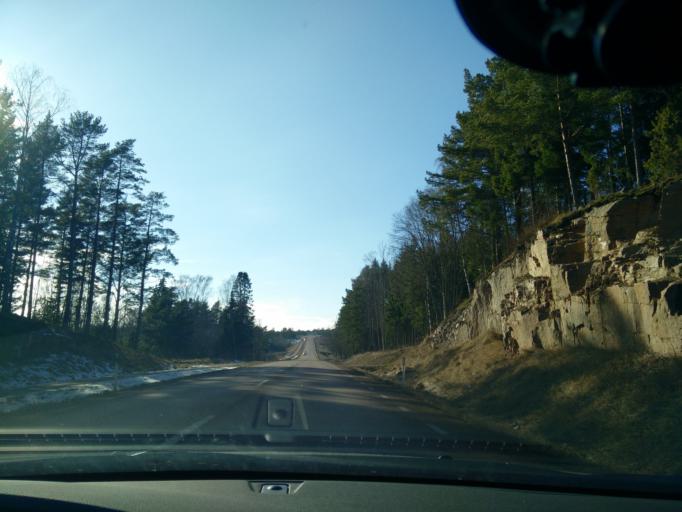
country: AX
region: Alands landsbygd
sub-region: Eckeroe
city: Eckeroe
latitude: 60.2156
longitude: 19.6681
